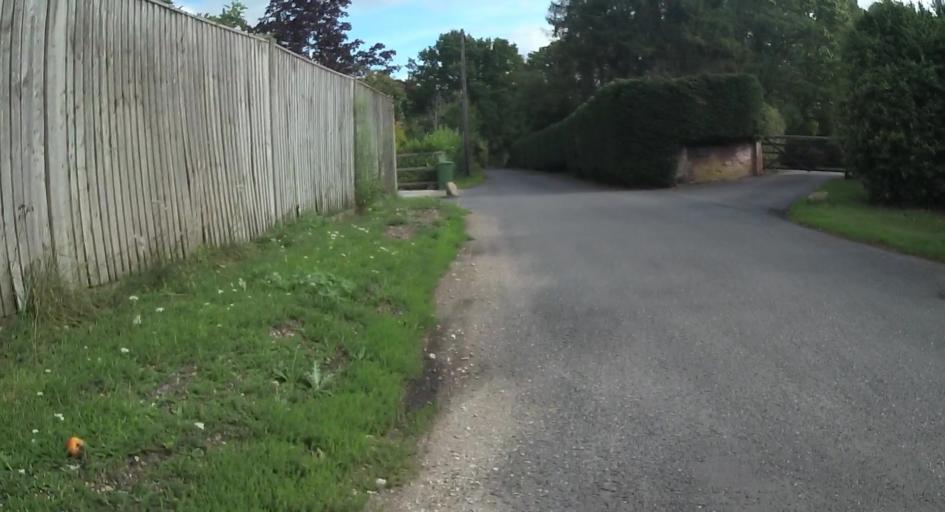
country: GB
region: England
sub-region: West Berkshire
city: Thatcham
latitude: 51.3752
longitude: -1.2160
